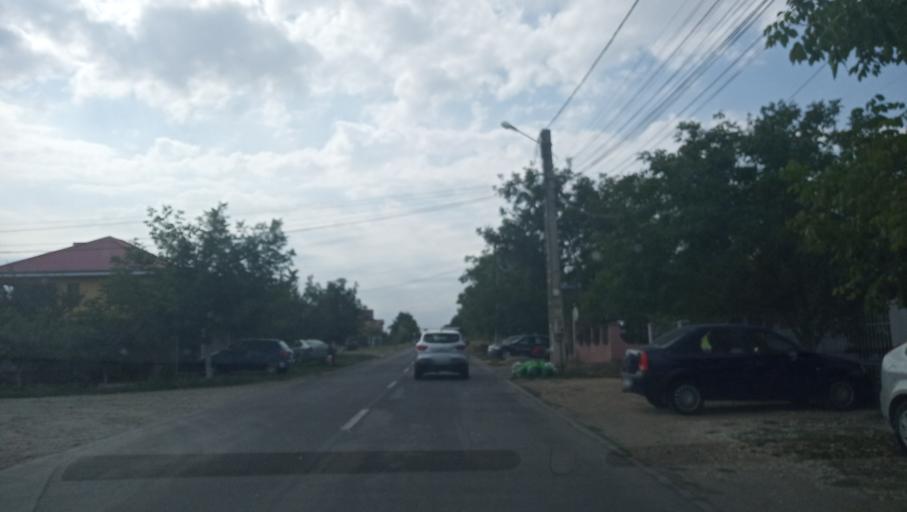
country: RO
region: Constanta
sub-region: Municipiul Mangalia
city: Mangalia
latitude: 43.8155
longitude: 28.5634
